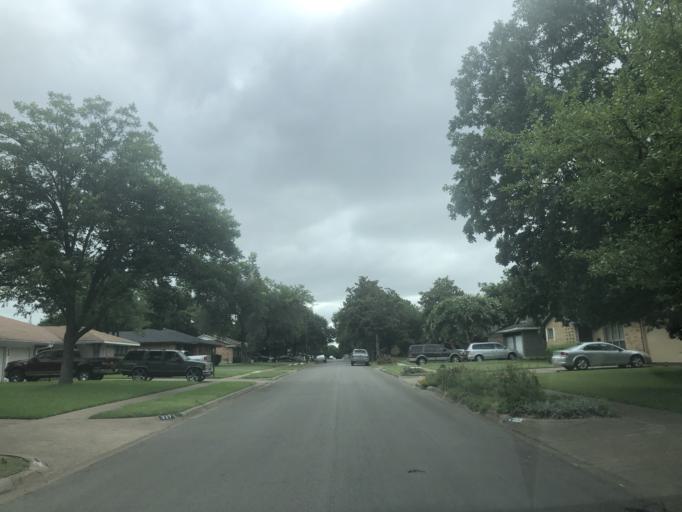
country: US
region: Texas
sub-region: Dallas County
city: Duncanville
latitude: 32.6563
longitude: -96.9152
